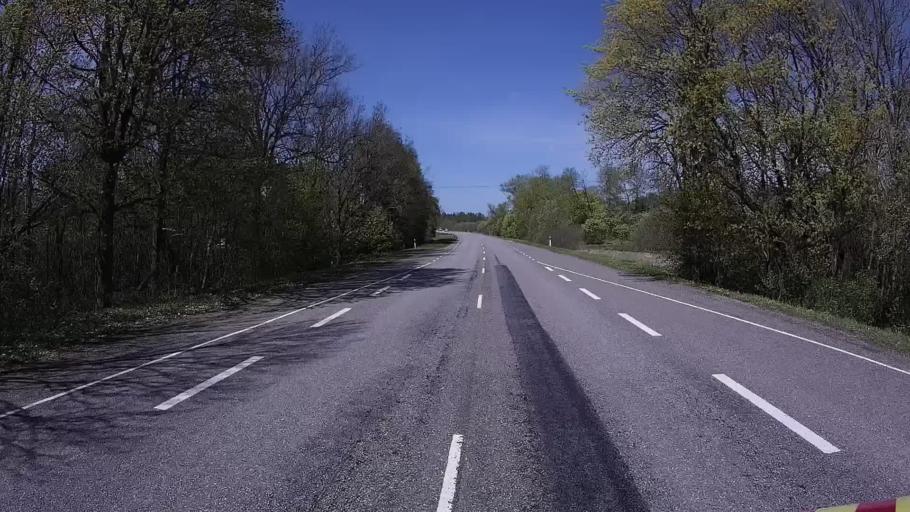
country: EE
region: Laeaene
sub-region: Lihula vald
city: Lihula
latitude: 58.7817
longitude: 23.9061
